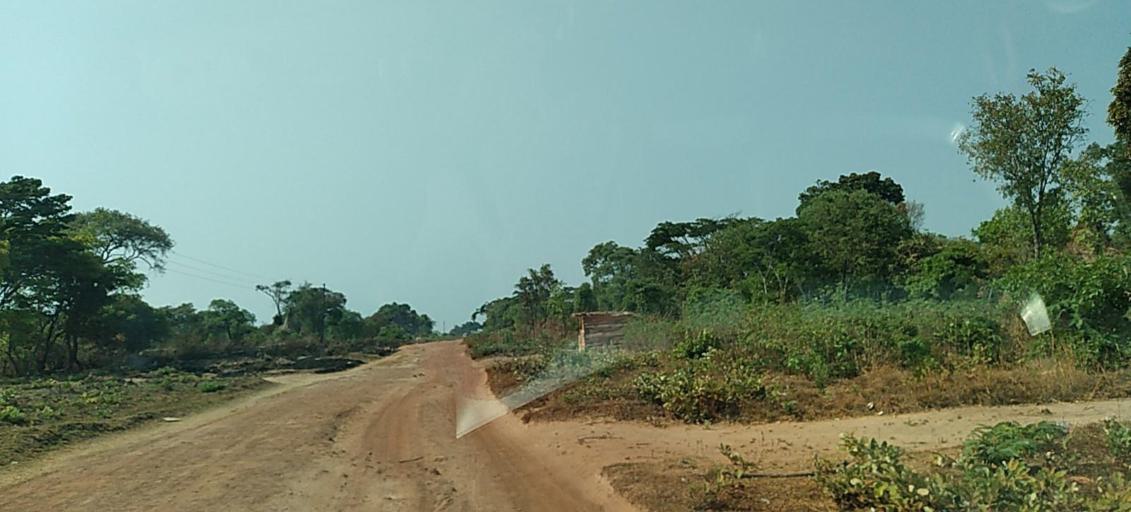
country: ZM
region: Copperbelt
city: Chingola
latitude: -12.9159
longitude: 27.3731
